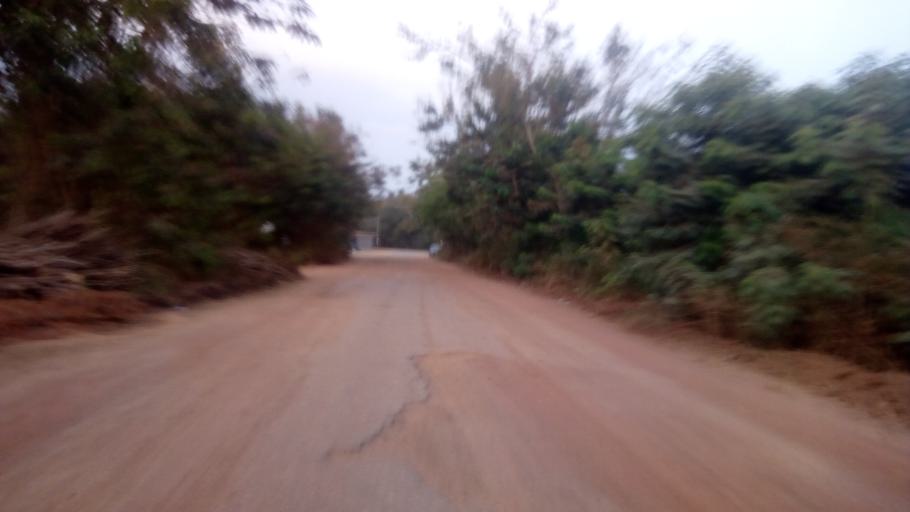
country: GH
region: Central
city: Cape Coast
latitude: 5.1188
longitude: -1.2737
